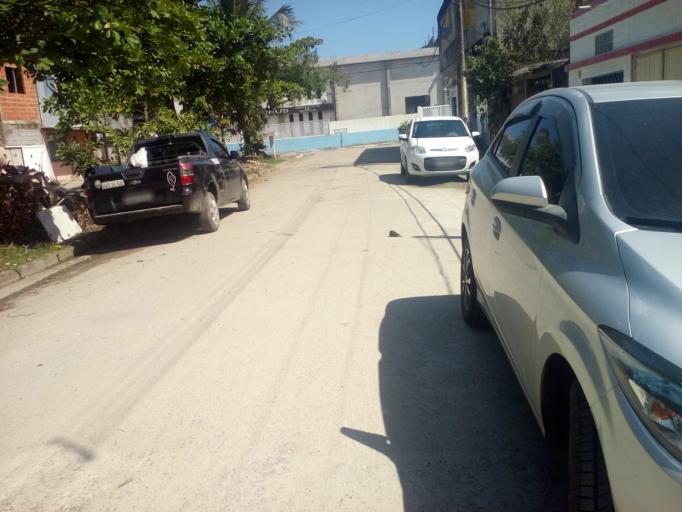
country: BR
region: Sao Paulo
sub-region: Guaruja
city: Guaruja
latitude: -23.9639
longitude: -46.2579
